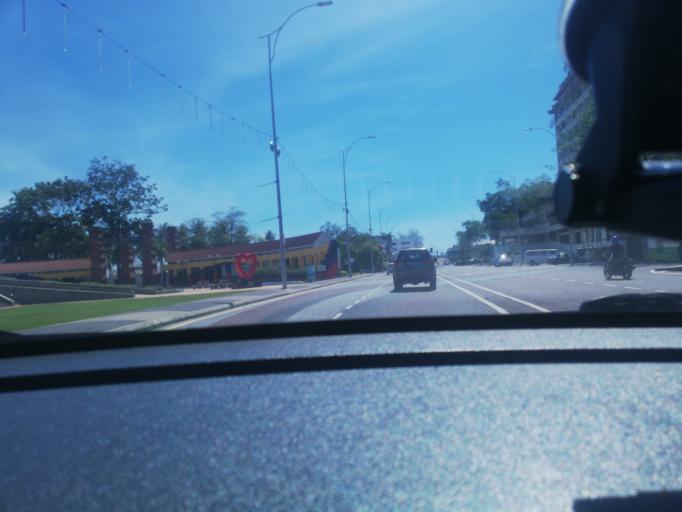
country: MY
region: Labuan
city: Victoria
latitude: 5.2764
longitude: 115.2452
